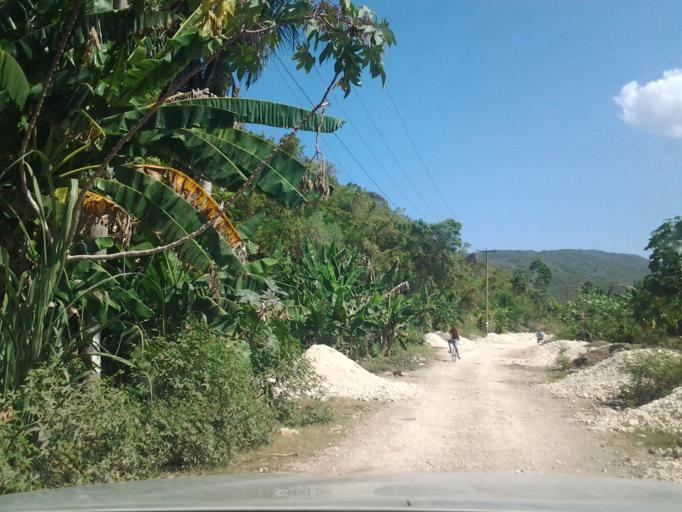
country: HT
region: Ouest
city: Tigwav
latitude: 18.4403
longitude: -72.8424
